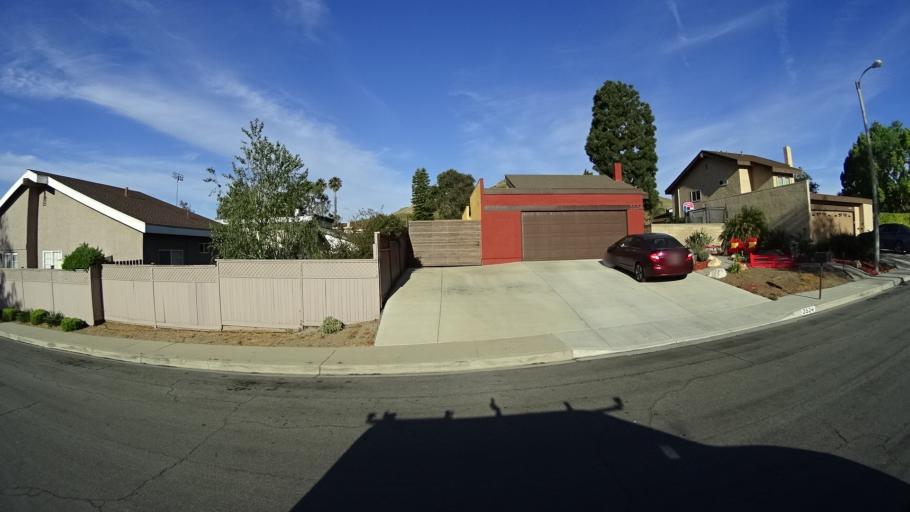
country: US
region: California
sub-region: Ventura County
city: Casa Conejo
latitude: 34.1870
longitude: -118.9505
